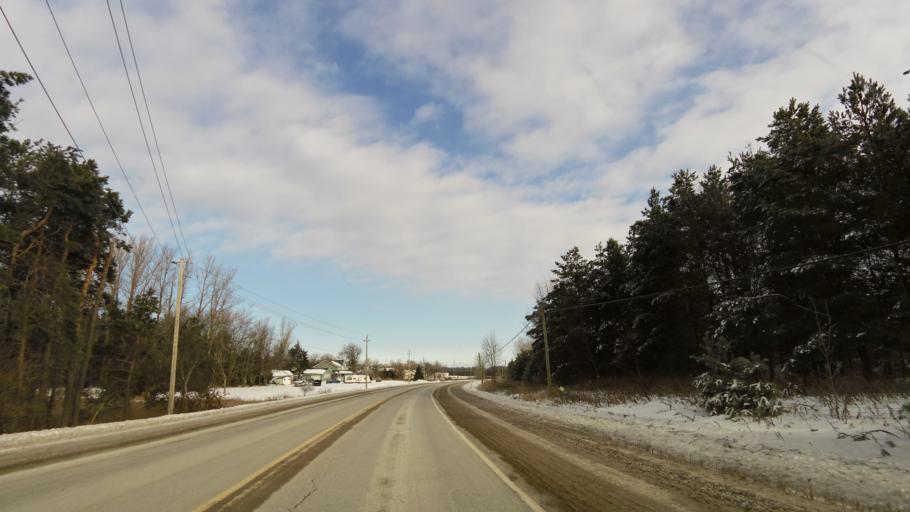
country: CA
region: Ontario
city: Quinte West
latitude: 44.0878
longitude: -77.7749
